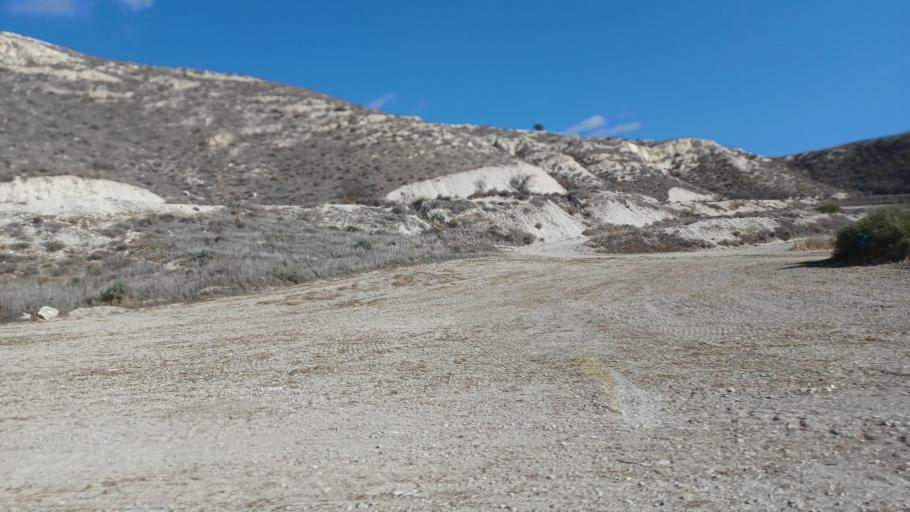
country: CY
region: Larnaka
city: Troulloi
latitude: 35.0308
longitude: 33.5784
